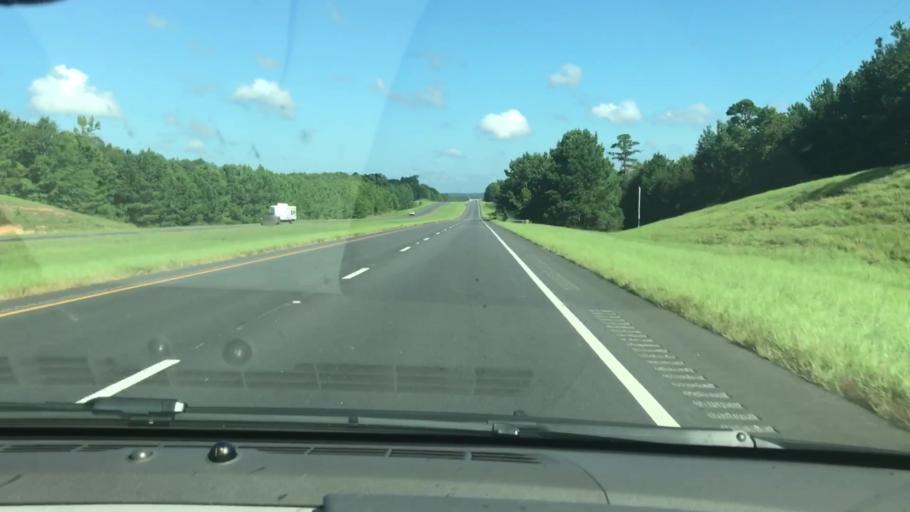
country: US
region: Alabama
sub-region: Barbour County
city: Eufaula
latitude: 32.0401
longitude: -85.1273
